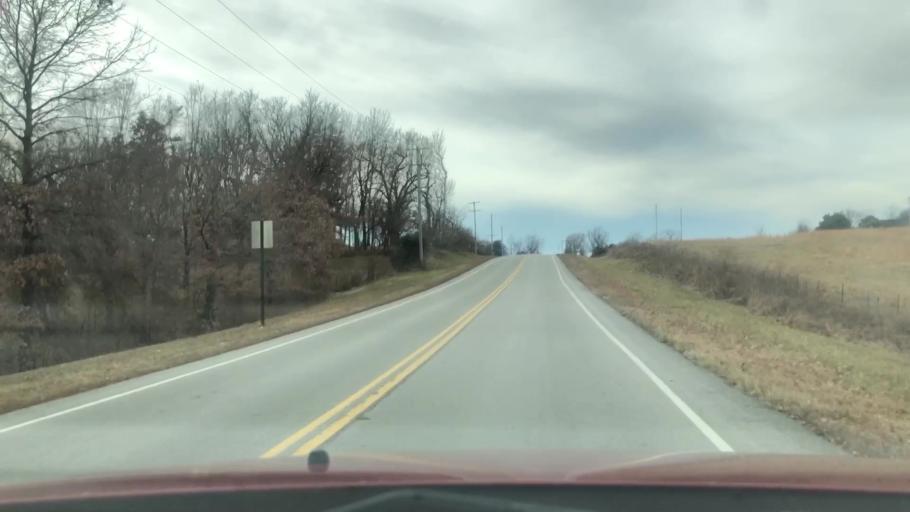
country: US
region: Missouri
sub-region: Greene County
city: Springfield
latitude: 37.2728
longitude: -93.2347
